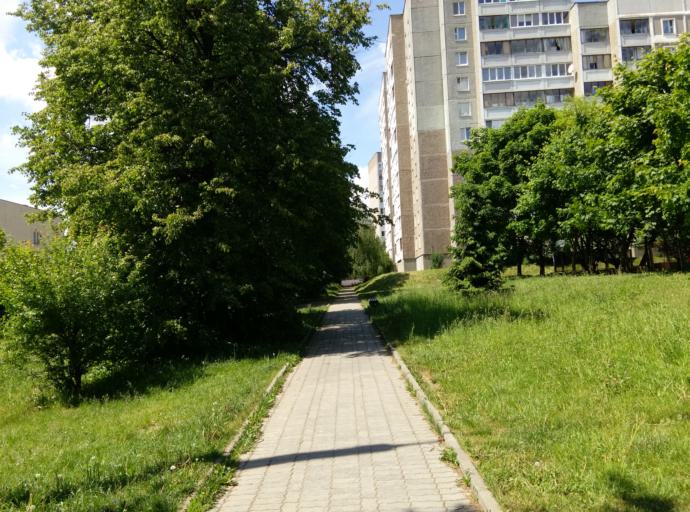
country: BY
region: Minsk
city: Minsk
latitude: 53.9225
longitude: 27.6336
